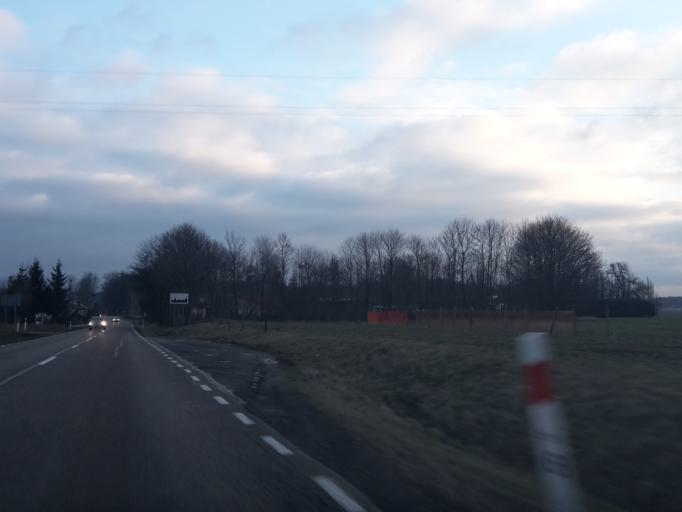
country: PL
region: Warmian-Masurian Voivodeship
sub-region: Powiat ilawski
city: Lubawa
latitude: 53.5938
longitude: 19.8524
